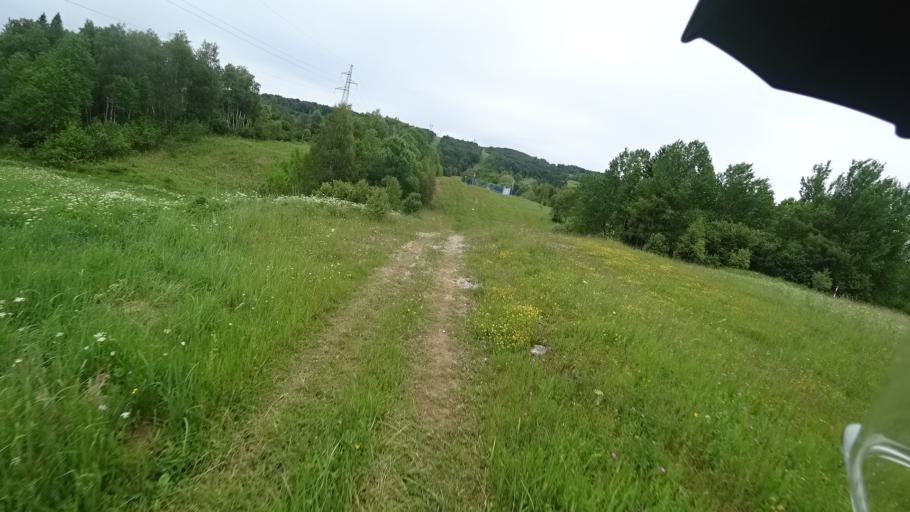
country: HR
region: Primorsko-Goranska
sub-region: Grad Delnice
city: Delnice
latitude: 45.3799
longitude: 14.8829
